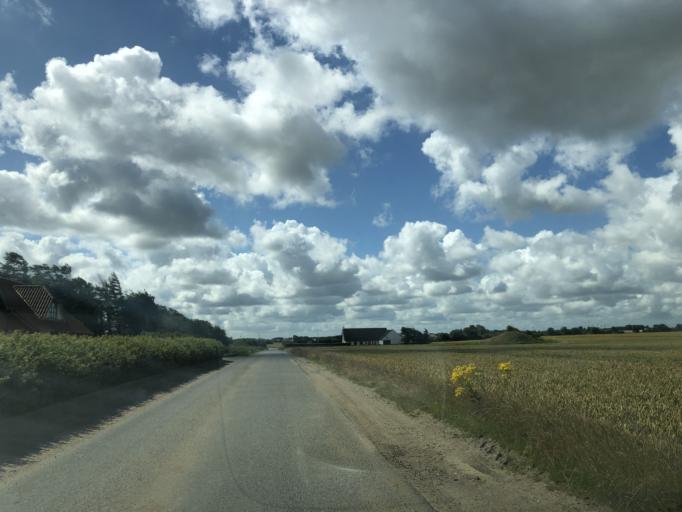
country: DK
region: Central Jutland
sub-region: Struer Kommune
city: Struer
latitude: 56.4757
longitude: 8.5218
